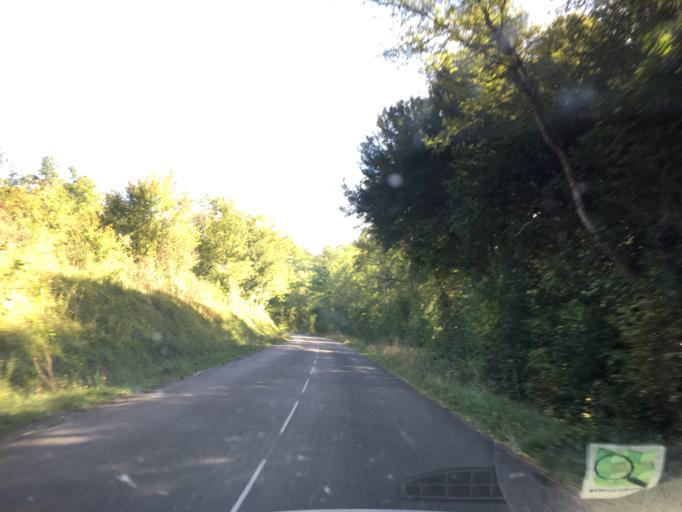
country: FR
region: Bourgogne
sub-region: Departement de l'Yonne
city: Vermenton
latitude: 47.5913
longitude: 3.6879
